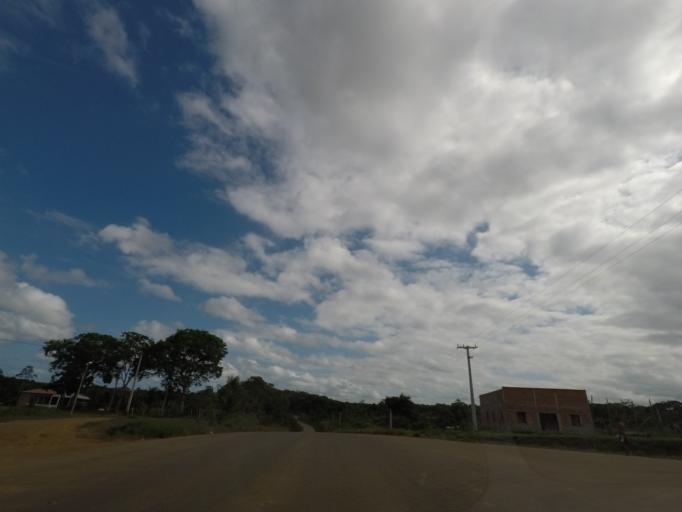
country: BR
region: Bahia
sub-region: Itacare
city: Itacare
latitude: -14.2134
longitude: -39.1011
